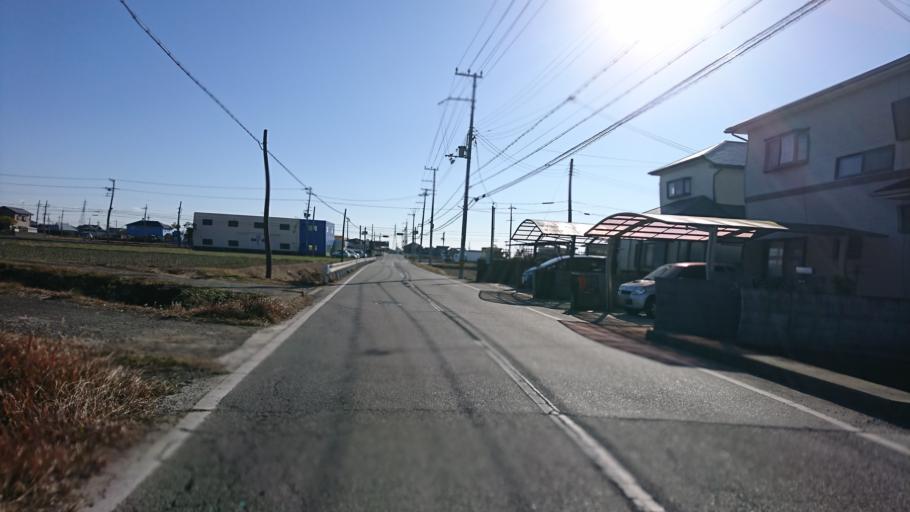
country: JP
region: Hyogo
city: Miki
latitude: 34.7491
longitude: 134.9300
